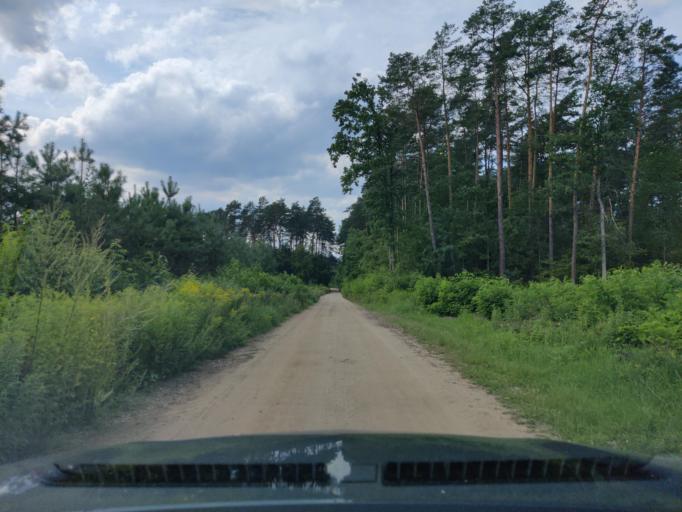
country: PL
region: Masovian Voivodeship
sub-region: Powiat pultuski
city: Obryte
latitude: 52.6901
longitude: 21.1702
